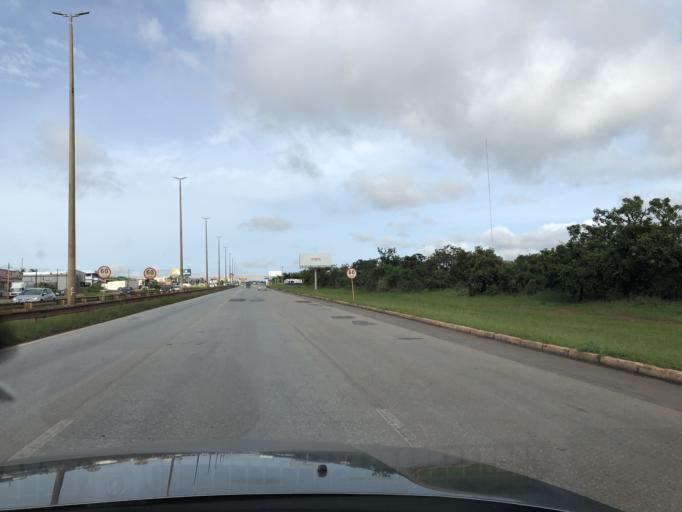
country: BR
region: Federal District
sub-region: Brasilia
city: Brasilia
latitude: -15.7877
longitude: -48.0132
